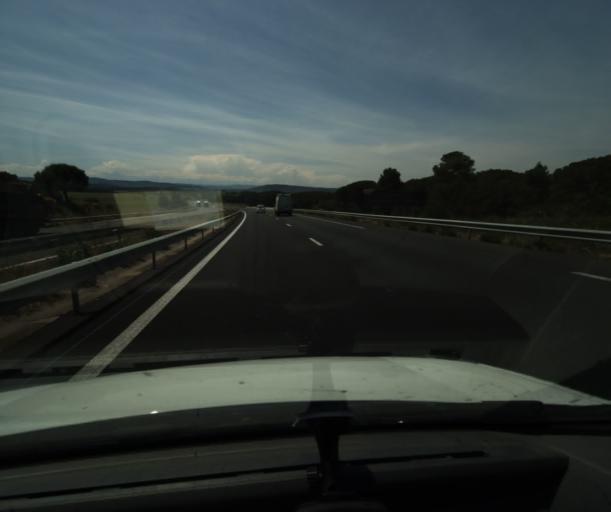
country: FR
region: Languedoc-Roussillon
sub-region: Departement de l'Aude
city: Bizanet
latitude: 43.1560
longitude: 2.8893
